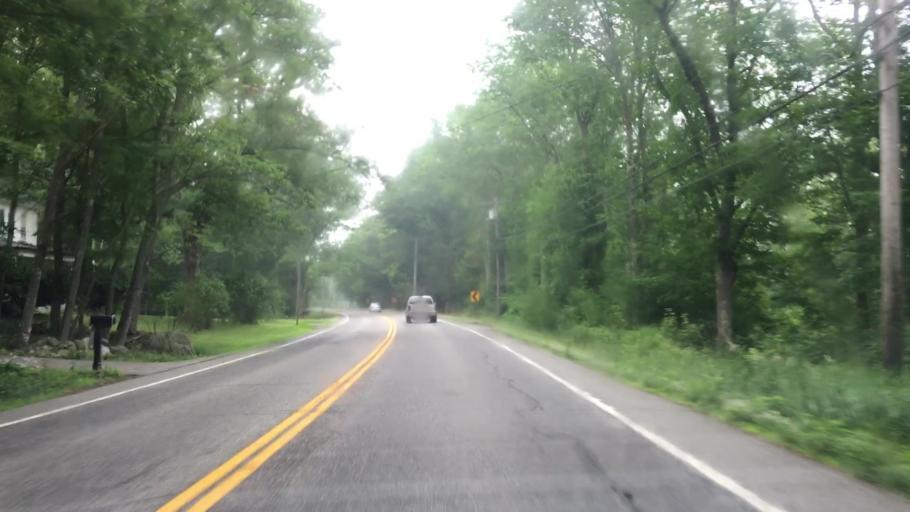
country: US
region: Maine
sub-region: Lincoln County
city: Wiscasset
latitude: 43.9911
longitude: -69.6391
